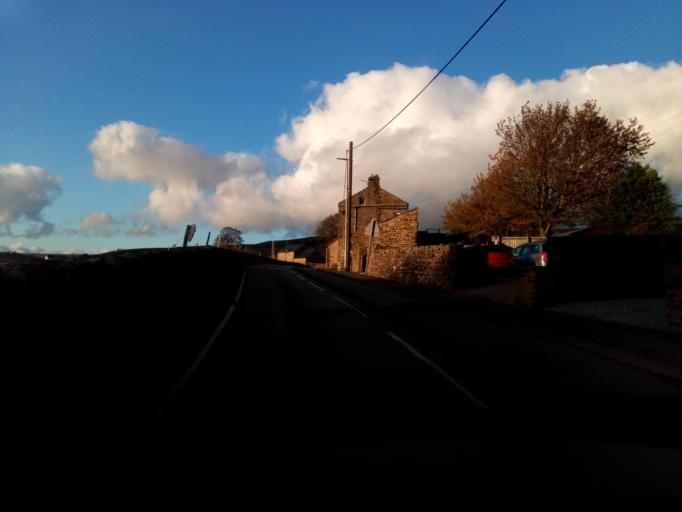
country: GB
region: England
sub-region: County Durham
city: Newbiggin
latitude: 54.7438
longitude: -2.2089
